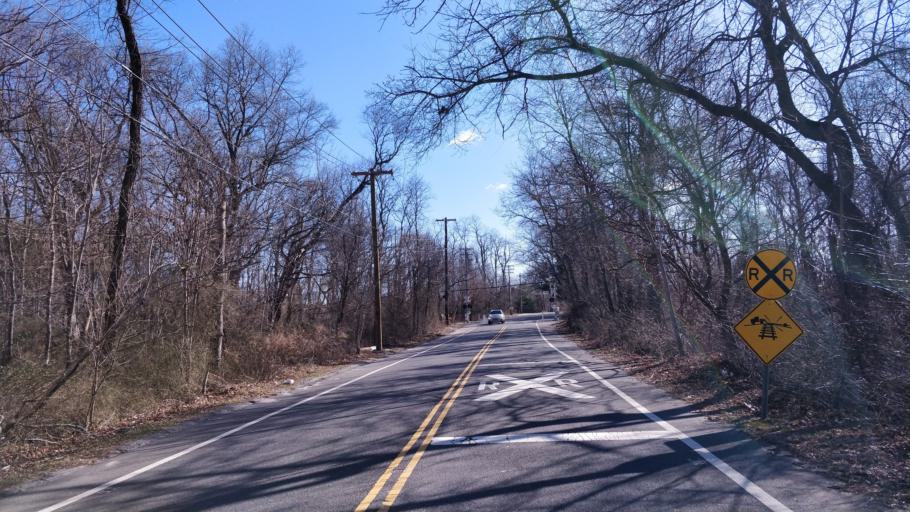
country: US
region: New York
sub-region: Suffolk County
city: Port Jefferson
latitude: 40.9370
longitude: -73.0832
